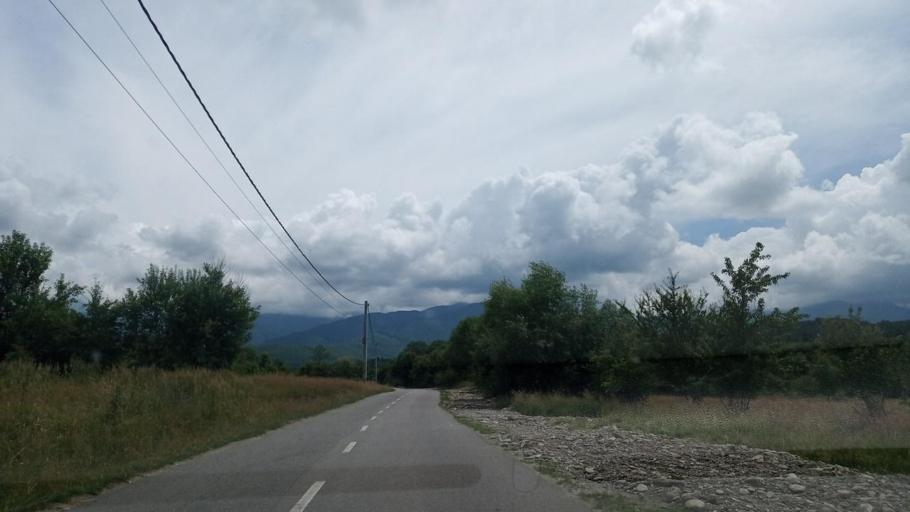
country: RO
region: Sibiu
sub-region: Comuna Porumbacu de Jos
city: Porumbacu de Jos
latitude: 45.6987
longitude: 24.4906
